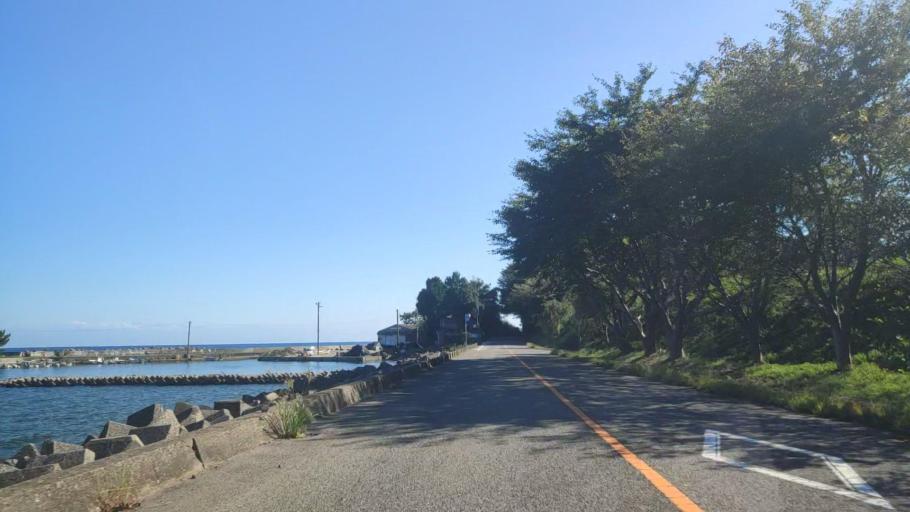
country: JP
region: Ishikawa
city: Nanao
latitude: 37.2751
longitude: 137.0968
